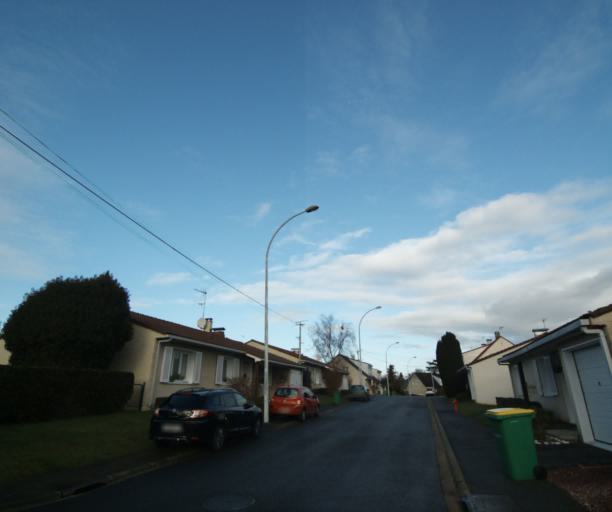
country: FR
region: Pays de la Loire
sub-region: Departement de la Sarthe
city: La Chapelle-Saint-Aubin
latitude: 48.0220
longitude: 0.1760
